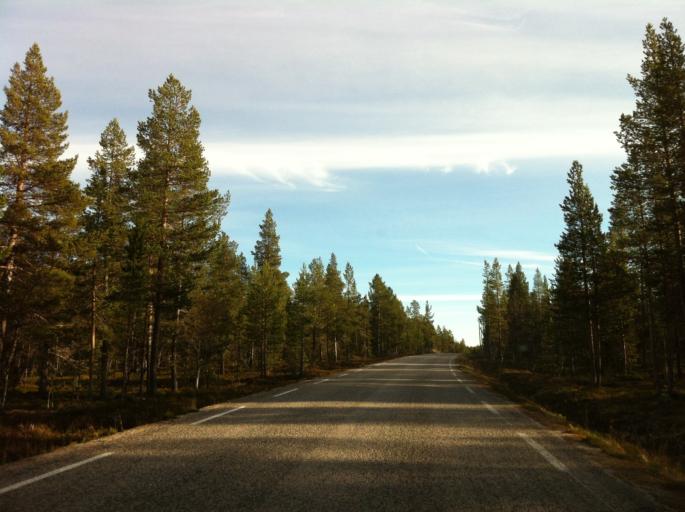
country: NO
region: Hedmark
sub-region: Engerdal
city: Engerdal
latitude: 62.1479
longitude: 11.9559
